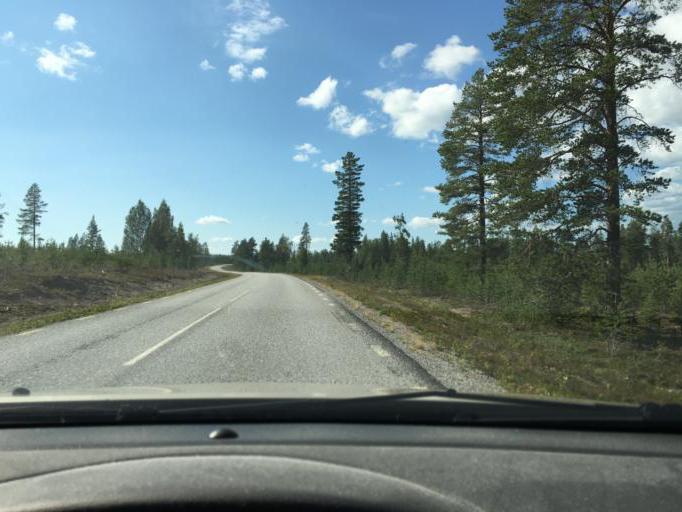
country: SE
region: Norrbotten
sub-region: Kalix Kommun
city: Toere
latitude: 66.0525
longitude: 22.4855
